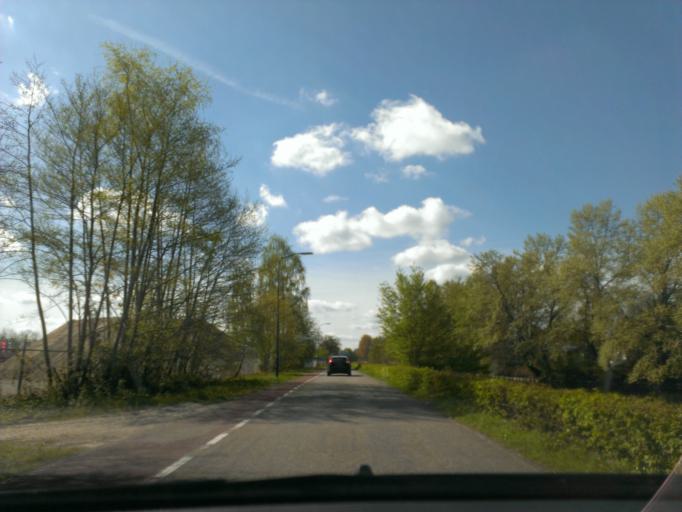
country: NL
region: Gelderland
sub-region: Gemeente Apeldoorn
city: Apeldoorn
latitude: 52.2290
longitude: 5.9749
